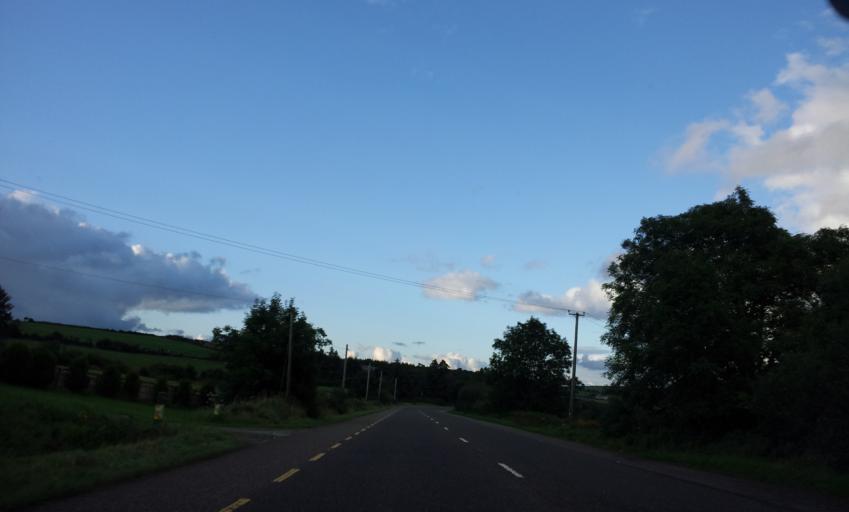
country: IE
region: Munster
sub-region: Ciarrai
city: Castleisland
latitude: 52.3014
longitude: -9.3825
